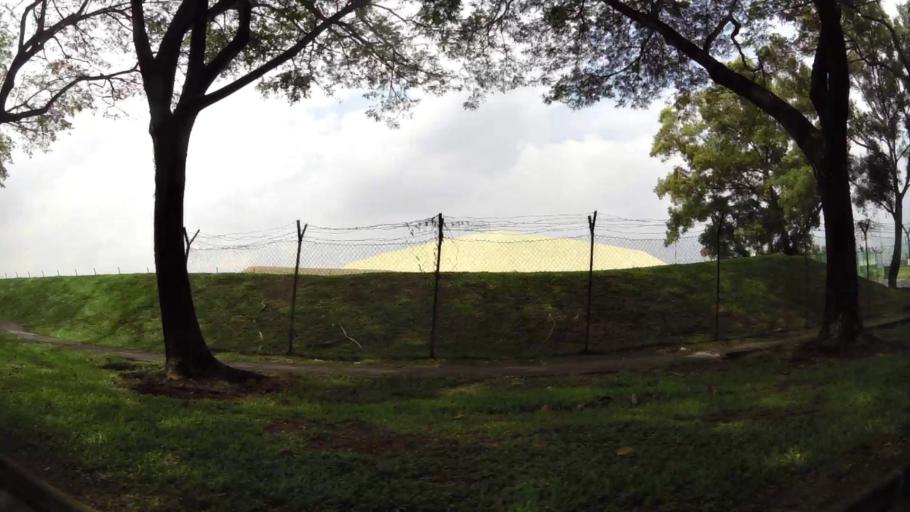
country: SG
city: Singapore
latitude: 1.3466
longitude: 103.9201
